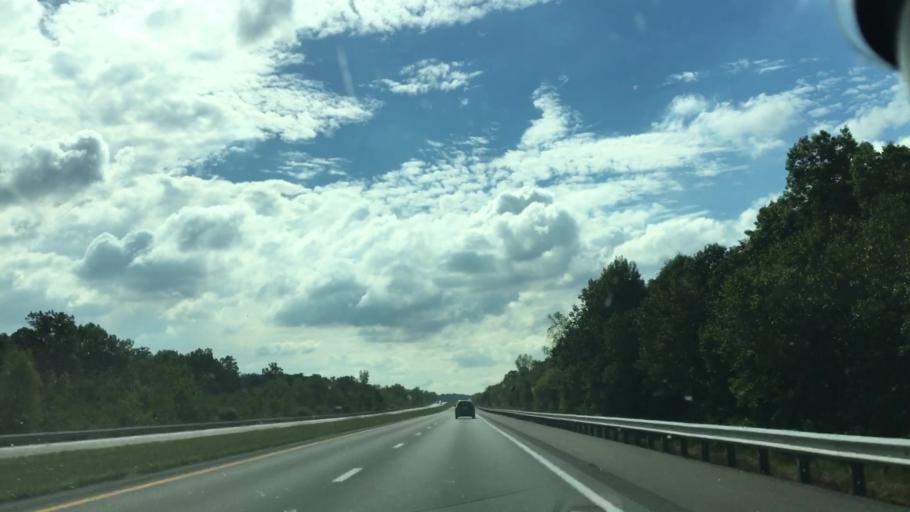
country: US
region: Kentucky
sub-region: Webster County
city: Sebree
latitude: 37.5884
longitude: -87.4904
